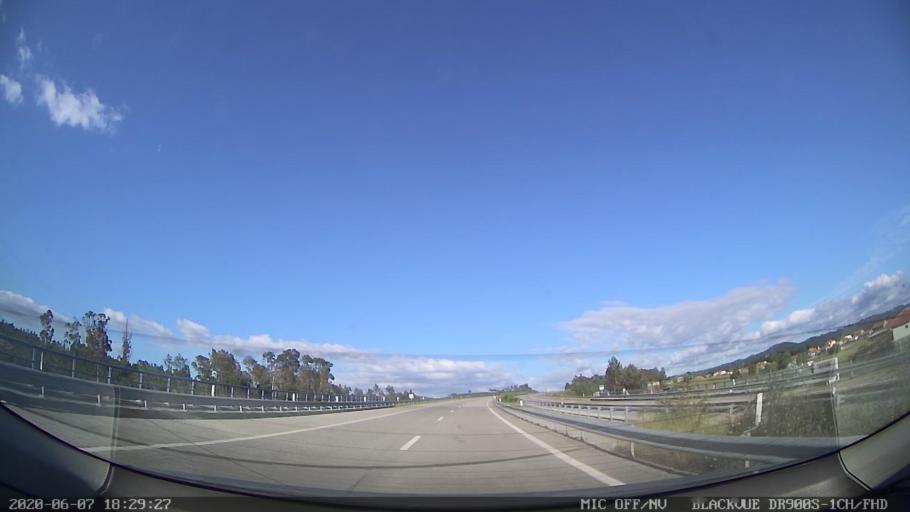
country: PT
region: Braga
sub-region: Fafe
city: Fafe
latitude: 41.4452
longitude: -8.0952
